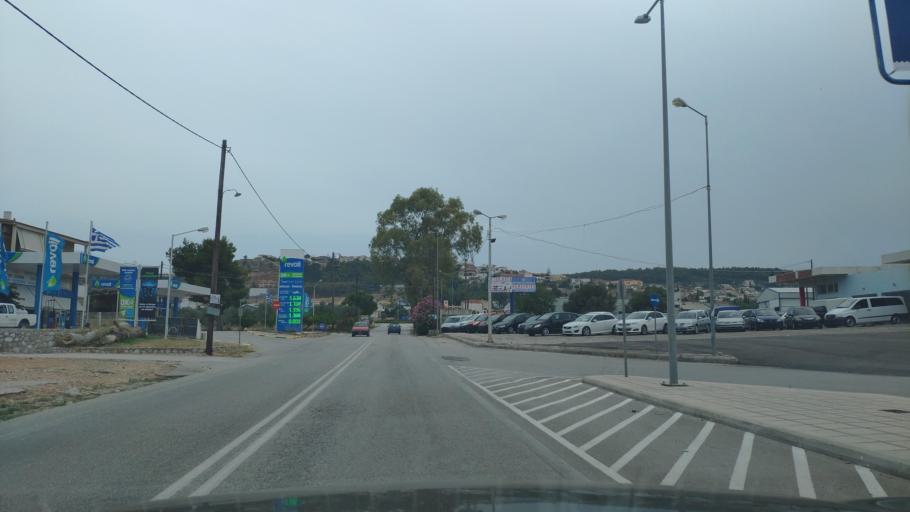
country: GR
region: Peloponnese
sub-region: Nomos Argolidos
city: Kranidi
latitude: 37.3899
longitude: 23.1579
